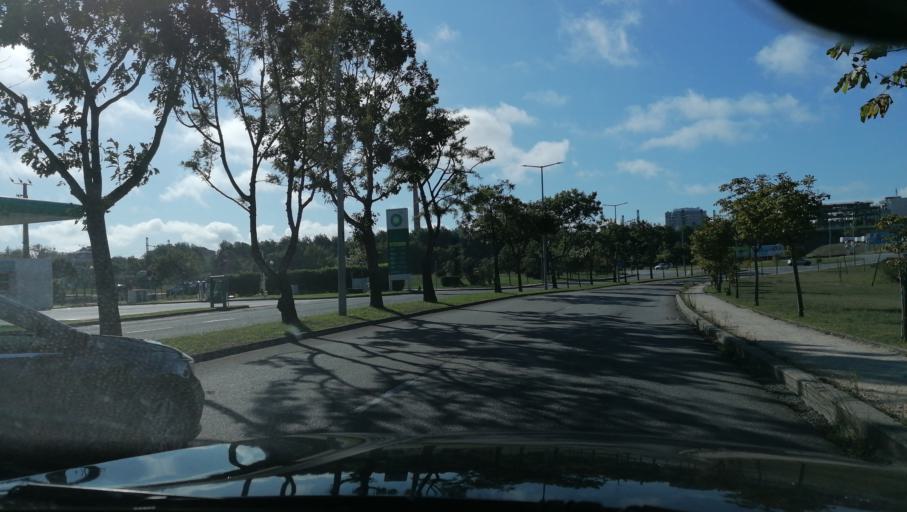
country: PT
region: Aveiro
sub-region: Aveiro
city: Aveiro
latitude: 40.6376
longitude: -8.6394
